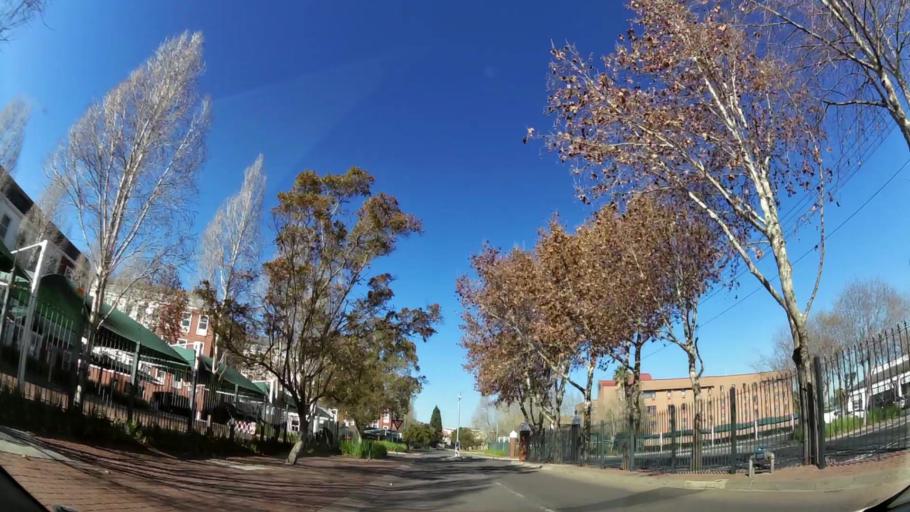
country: ZA
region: Gauteng
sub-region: City of Tshwane Metropolitan Municipality
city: Centurion
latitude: -25.8568
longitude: 28.2177
